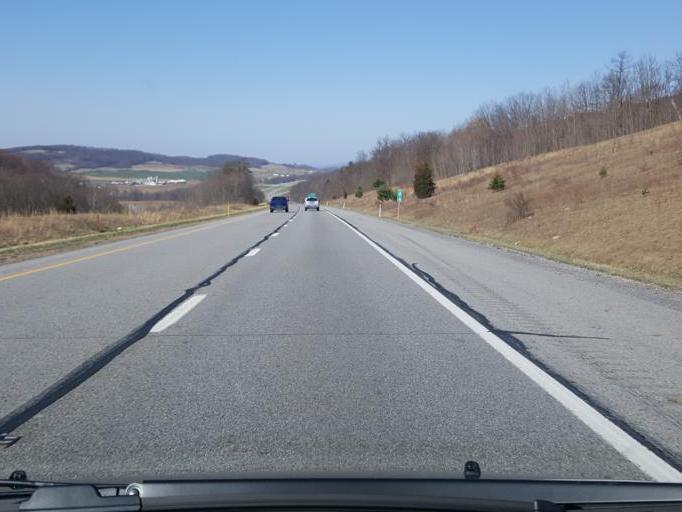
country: US
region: Pennsylvania
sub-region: Blair County
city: Claysburg
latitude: 40.1714
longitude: -78.4938
